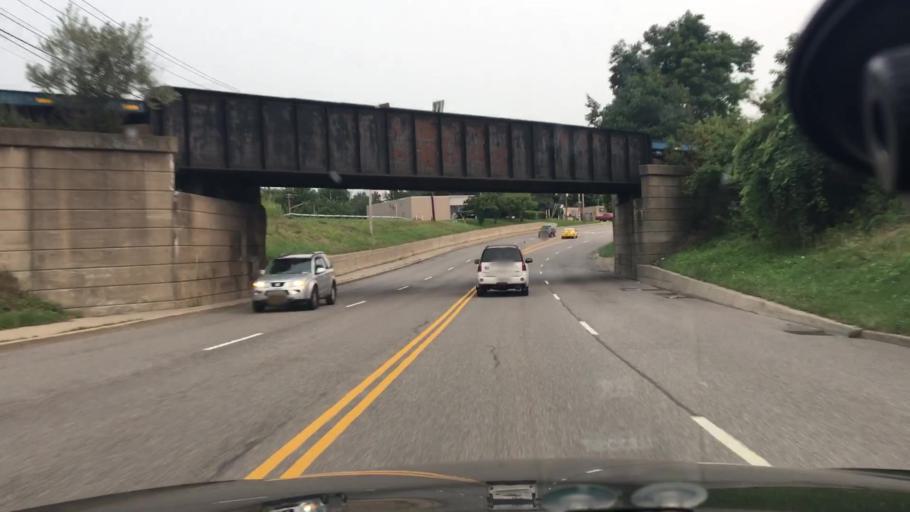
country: US
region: New York
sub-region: Erie County
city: Hamburg
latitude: 42.7321
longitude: -78.8357
